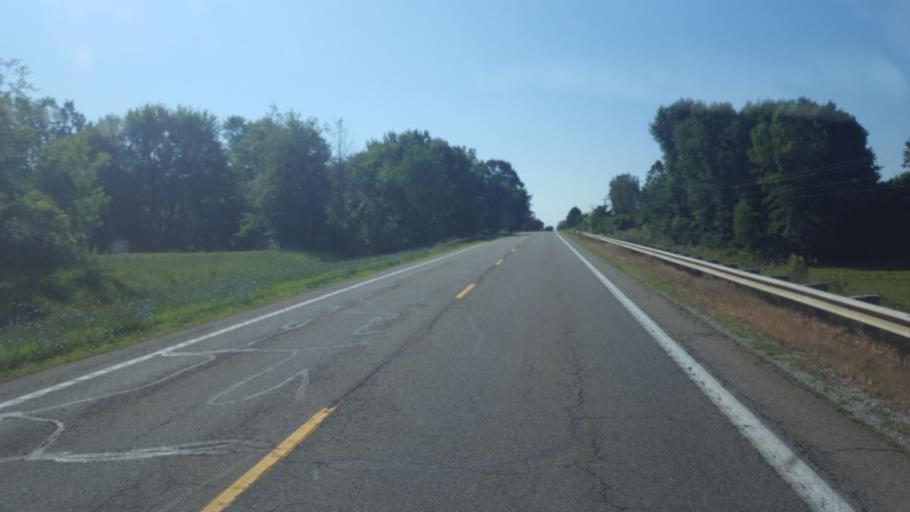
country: US
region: Ohio
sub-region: Morrow County
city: Mount Gilead
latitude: 40.5204
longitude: -82.7503
